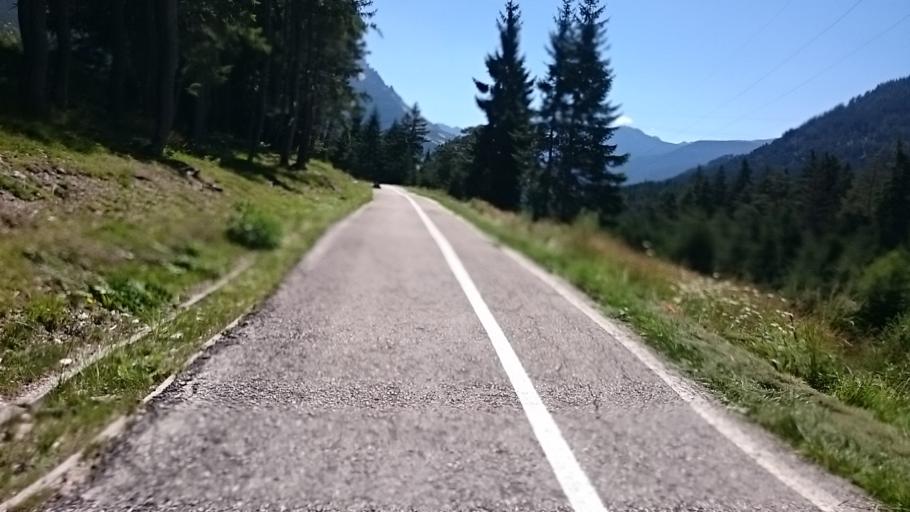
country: IT
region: Veneto
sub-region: Provincia di Belluno
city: San Vito
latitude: 46.4881
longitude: 12.1859
